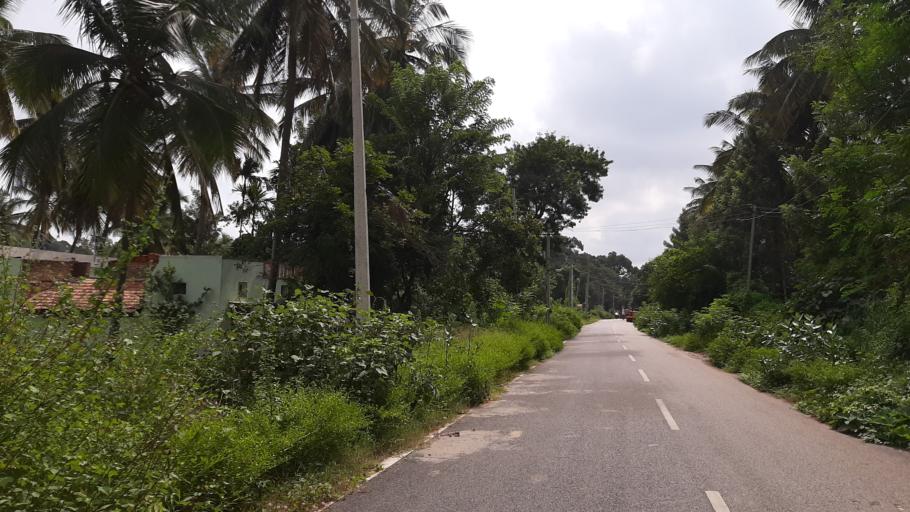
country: IN
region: Karnataka
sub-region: Ramanagara
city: Magadi
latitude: 12.9026
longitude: 77.2841
